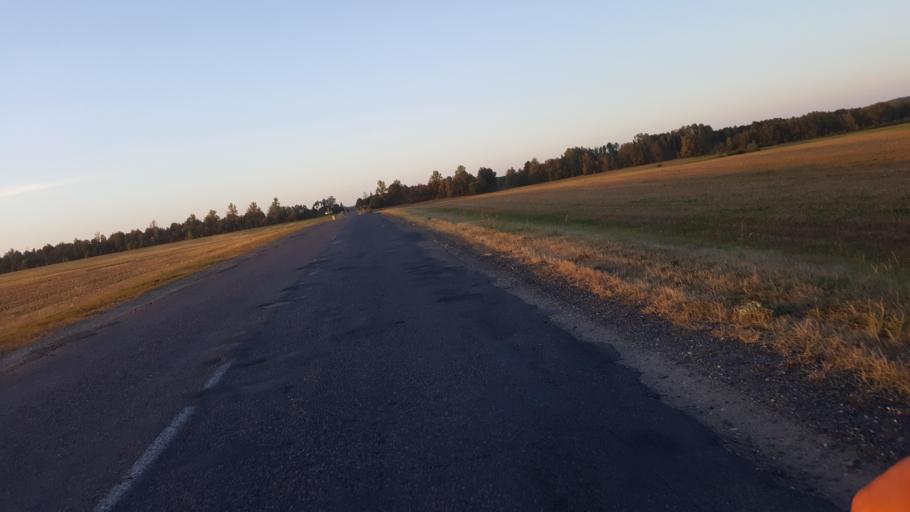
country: BY
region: Brest
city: Charnawchytsy
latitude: 52.3055
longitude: 23.6070
